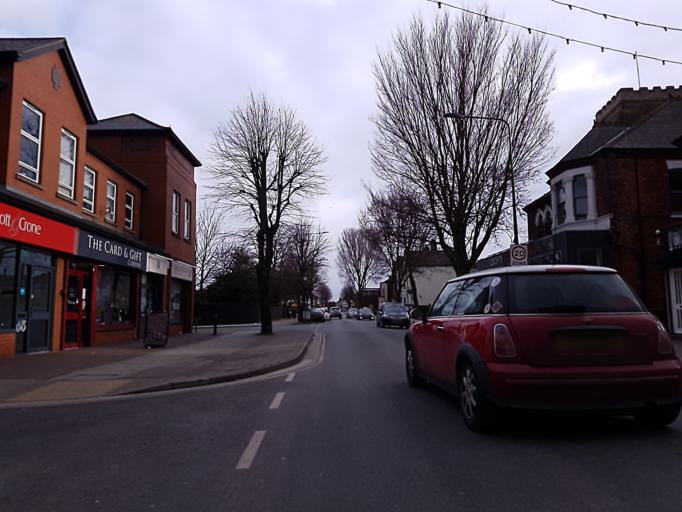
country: GB
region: England
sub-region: North East Lincolnshire
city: Cleethorpes
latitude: 53.5586
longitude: -0.0308
